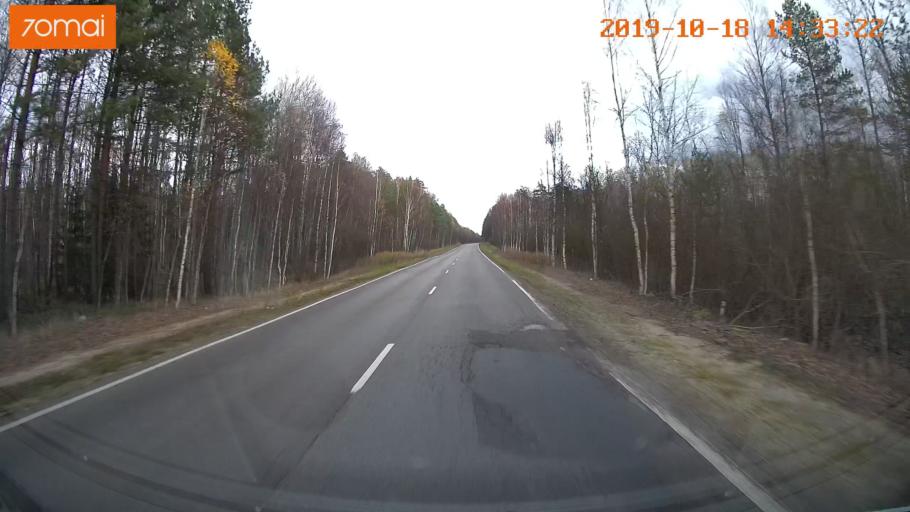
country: RU
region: Rjazan
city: Tuma
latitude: 55.2005
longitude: 40.5954
